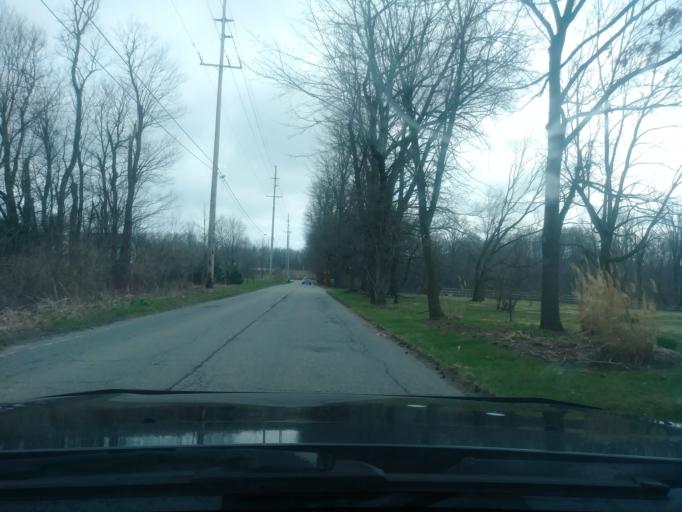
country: US
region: Indiana
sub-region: LaPorte County
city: LaPorte
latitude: 41.6323
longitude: -86.7968
